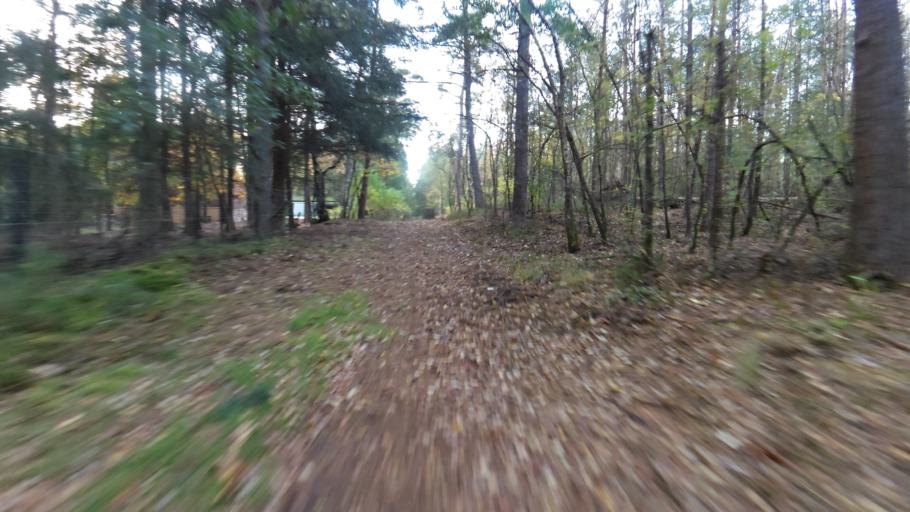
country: NL
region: Gelderland
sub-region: Gemeente Epe
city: Epe
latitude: 52.3695
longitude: 5.9466
